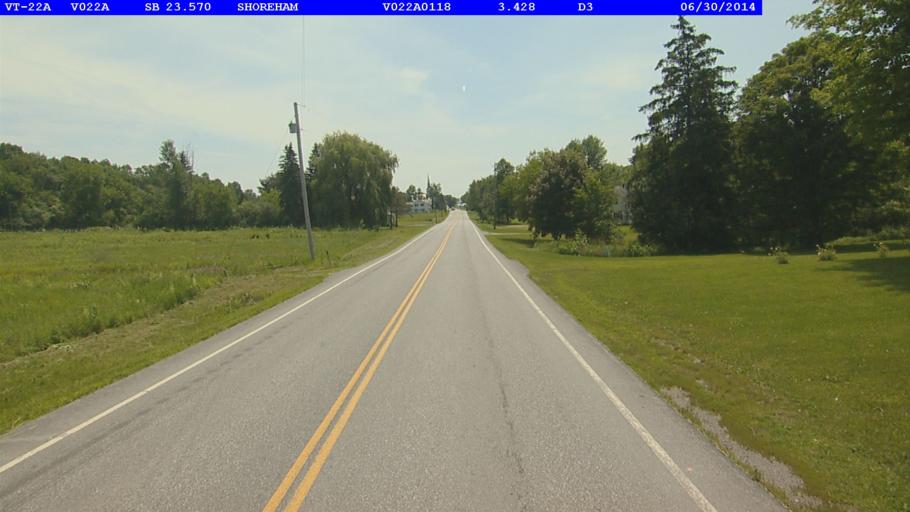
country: US
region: New York
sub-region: Essex County
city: Ticonderoga
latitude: 43.8988
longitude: -73.3085
